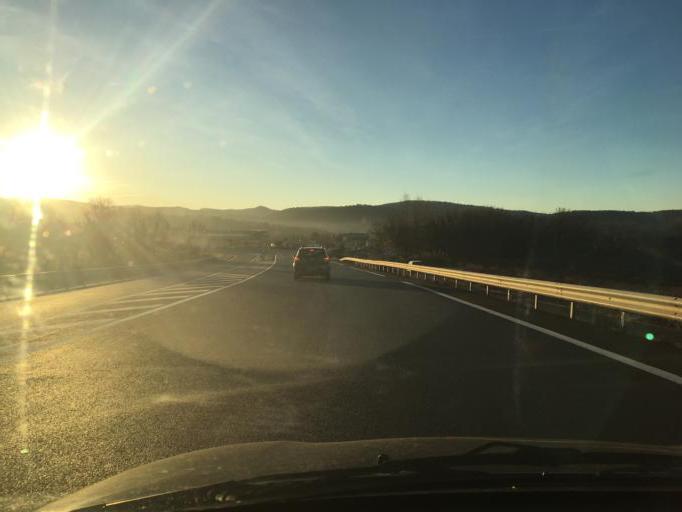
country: FR
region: Provence-Alpes-Cote d'Azur
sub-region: Departement du Var
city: Les Arcs
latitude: 43.4552
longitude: 6.4894
